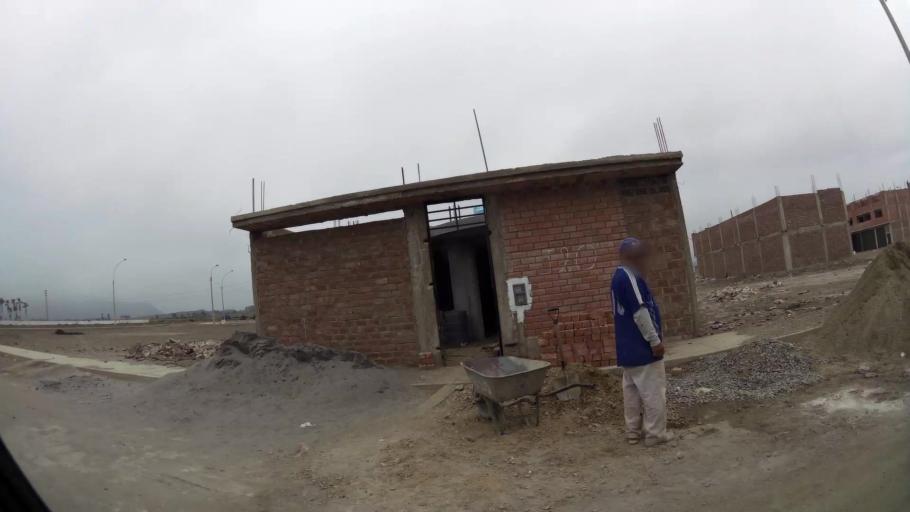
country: PE
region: Lima
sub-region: Barranca
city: Barranca
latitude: -10.7404
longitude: -77.7644
